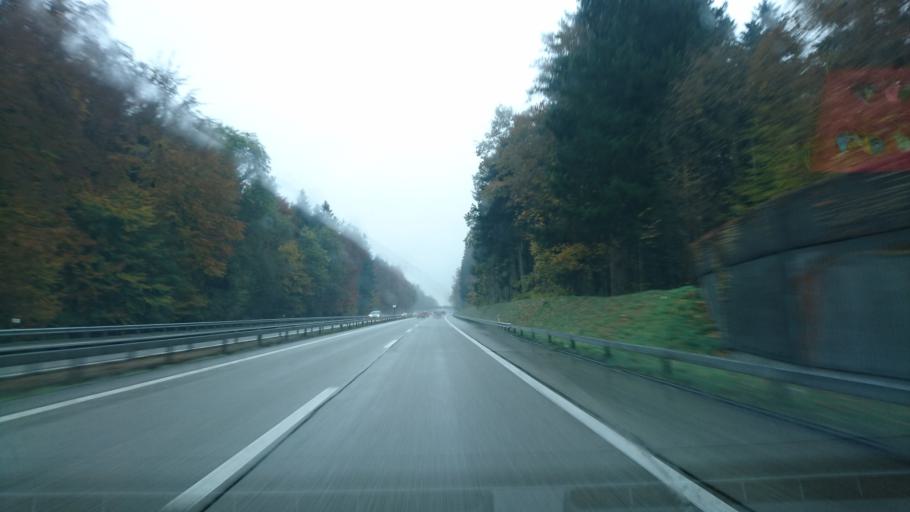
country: CH
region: Solothurn
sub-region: Bezirk Wasseramt
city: Kriegstetten
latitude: 47.1779
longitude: 7.5920
